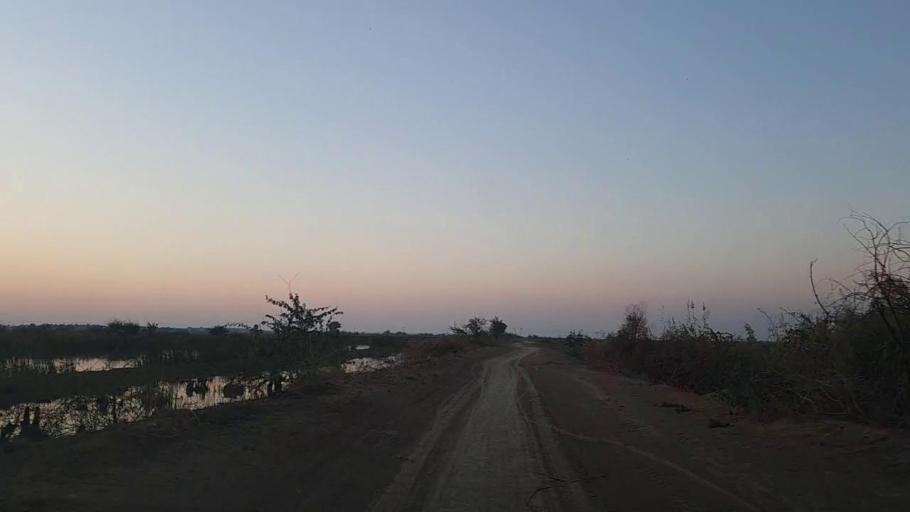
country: PK
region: Sindh
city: Tando Mittha Khan
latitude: 26.0653
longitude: 69.1615
